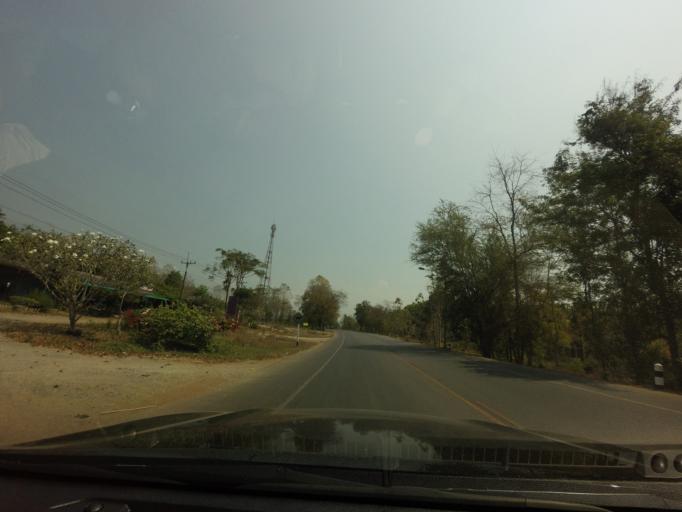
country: TH
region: Kanchanaburi
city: Thong Pha Phum
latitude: 14.6395
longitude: 98.6872
